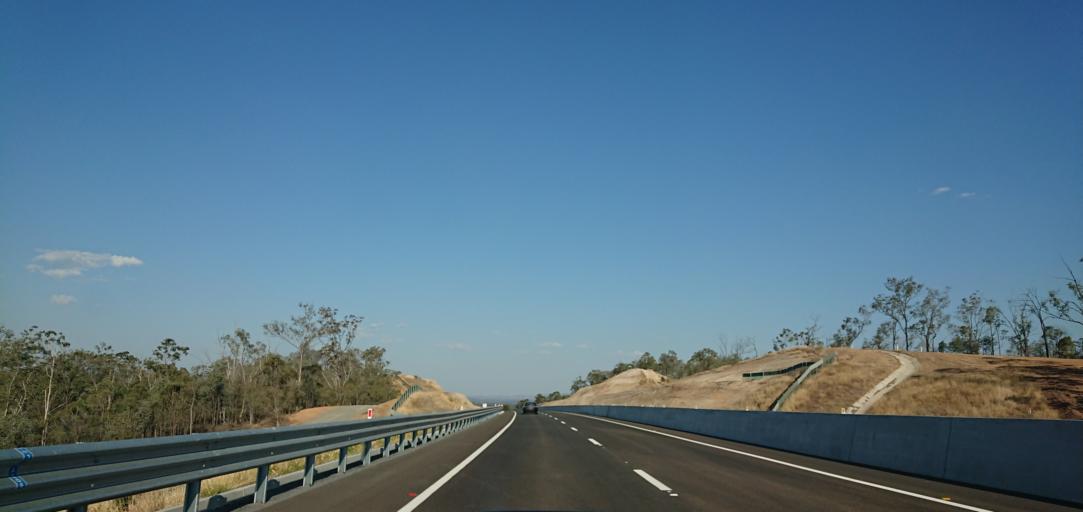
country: AU
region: Queensland
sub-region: Toowoomba
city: East Toowoomba
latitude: -27.5191
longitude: 152.0521
